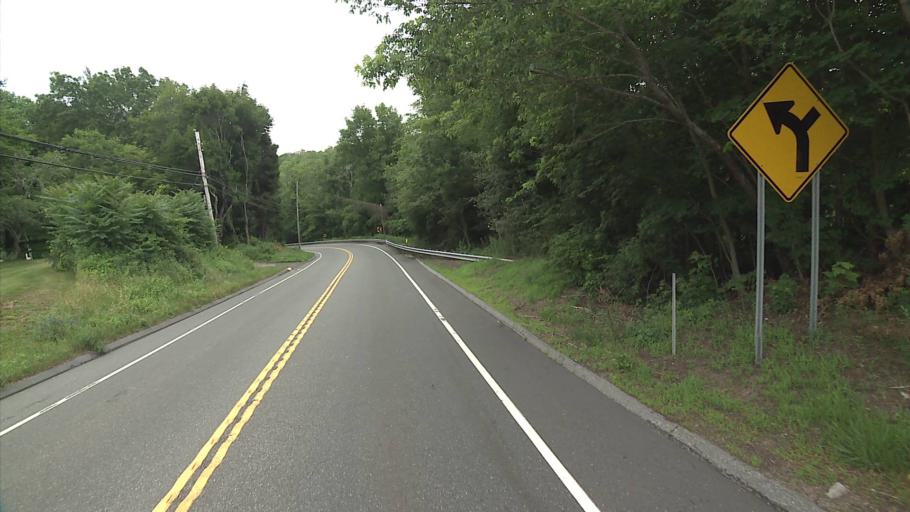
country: US
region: Connecticut
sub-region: New London County
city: Ledyard Center
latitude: 41.4704
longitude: -72.0249
